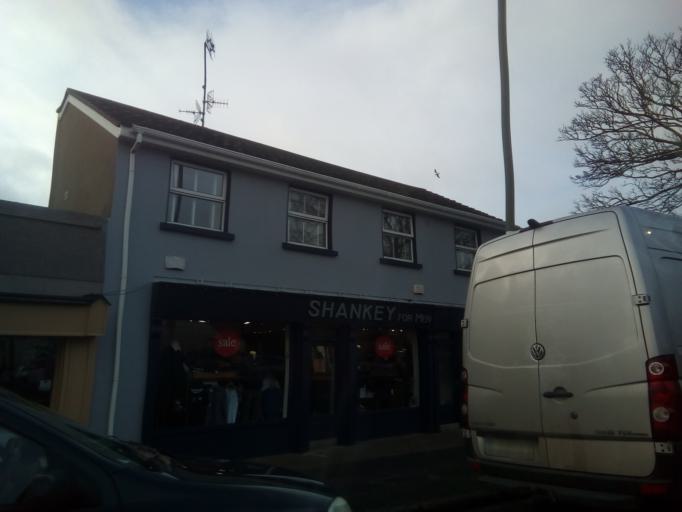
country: IE
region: Leinster
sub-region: Fingal County
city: Skerries
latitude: 53.5772
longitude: -6.1057
